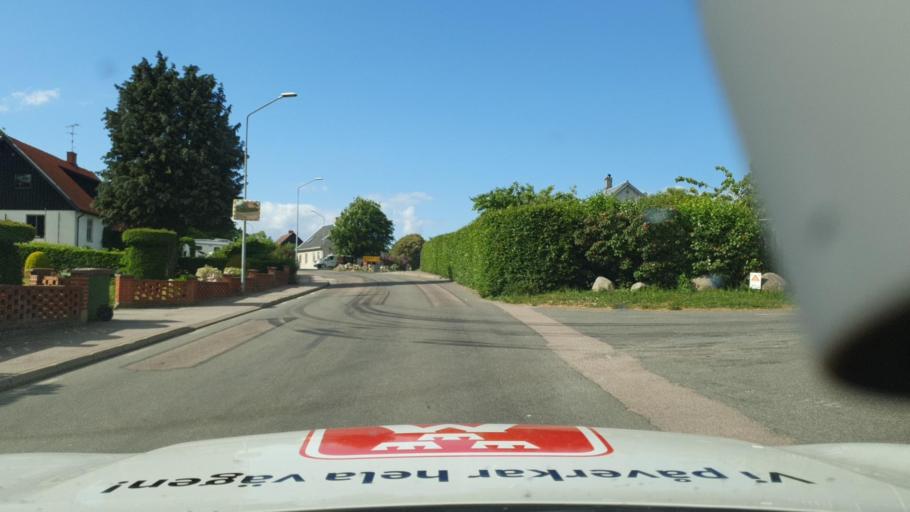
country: SE
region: Skane
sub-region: Simrishamns Kommun
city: Simrishamn
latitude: 55.5571
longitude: 14.3139
